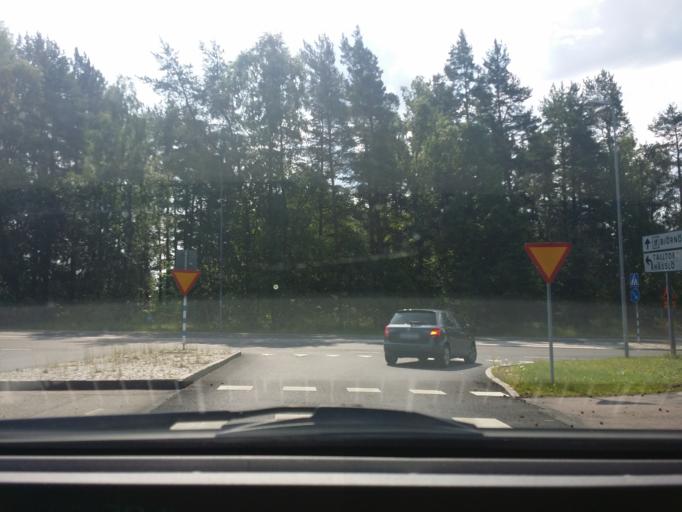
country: SE
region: Vaestmanland
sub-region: Vasteras
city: Vasteras
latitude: 59.6042
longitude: 16.5951
